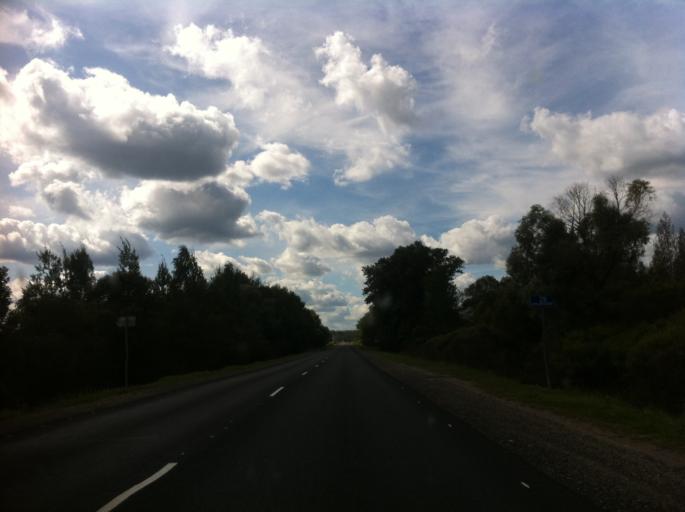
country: RU
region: Pskov
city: Izborsk
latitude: 57.7099
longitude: 27.8932
